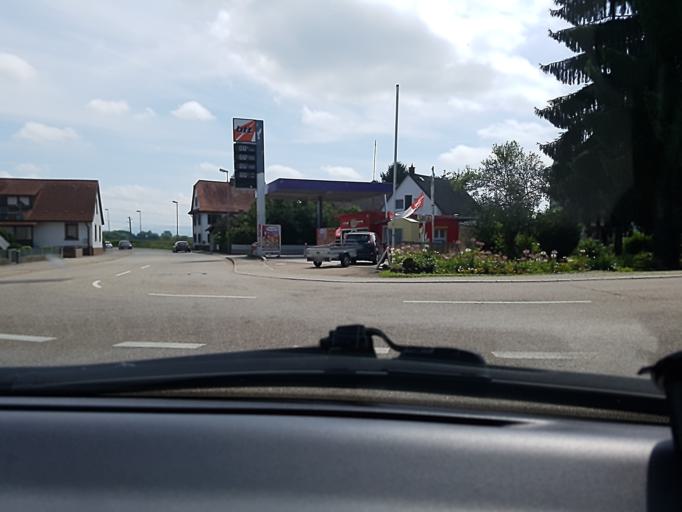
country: DE
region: Baden-Wuerttemberg
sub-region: Freiburg Region
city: Kehl
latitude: 48.5679
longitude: 7.8515
